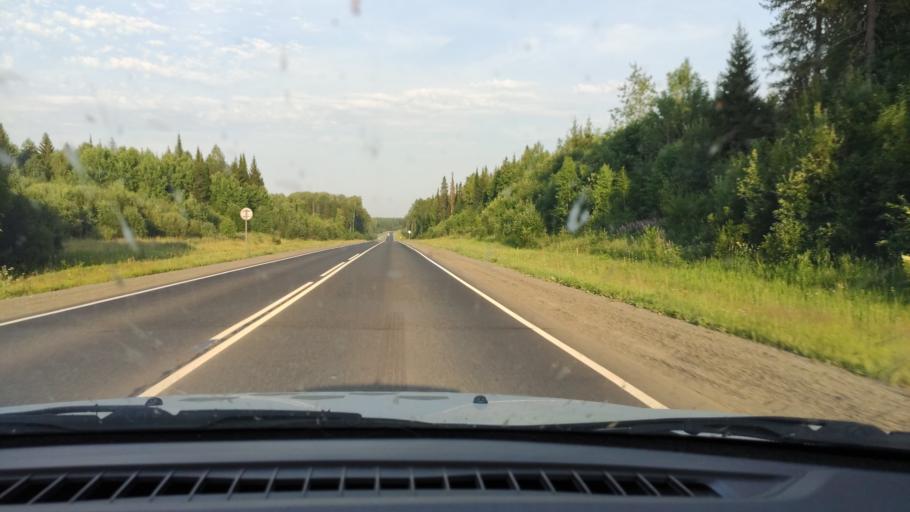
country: RU
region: Perm
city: Zyukayka
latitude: 58.3714
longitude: 54.6505
